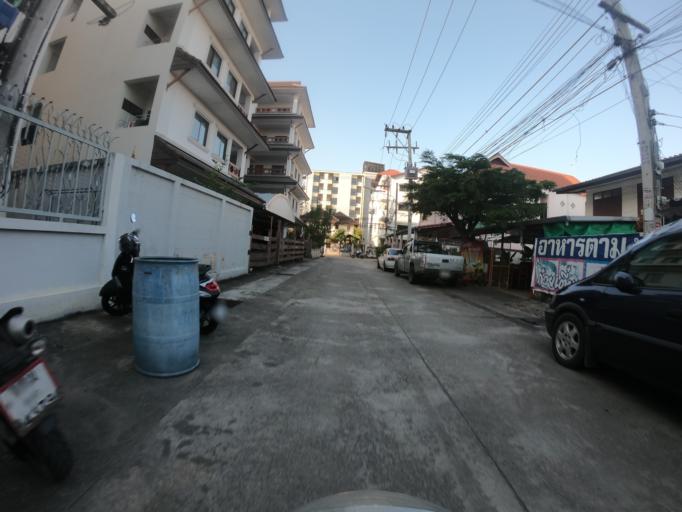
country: TH
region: Chiang Mai
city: Chiang Mai
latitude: 18.8063
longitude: 98.9917
